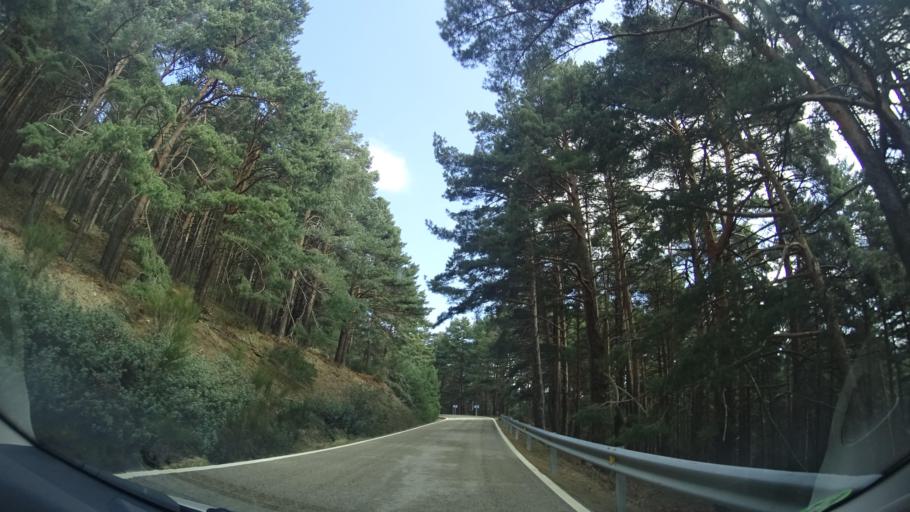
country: ES
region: Madrid
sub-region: Provincia de Madrid
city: Miraflores de la Sierra
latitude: 40.8583
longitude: -3.7658
